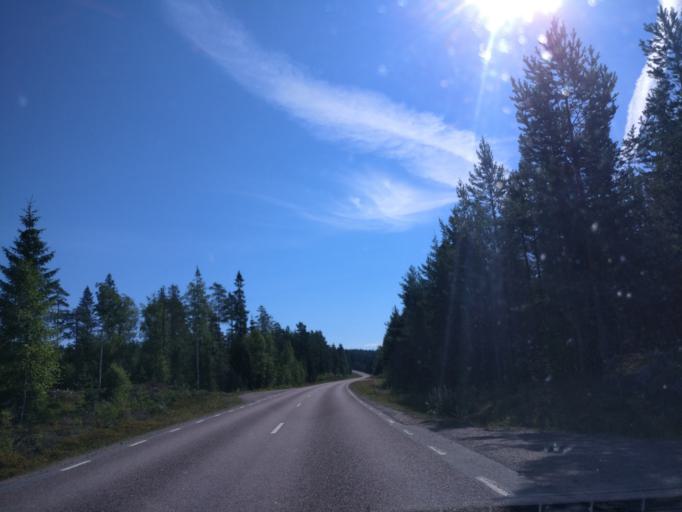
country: SE
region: Vaermland
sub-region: Filipstads Kommun
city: Lesjofors
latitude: 60.0462
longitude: 13.9656
